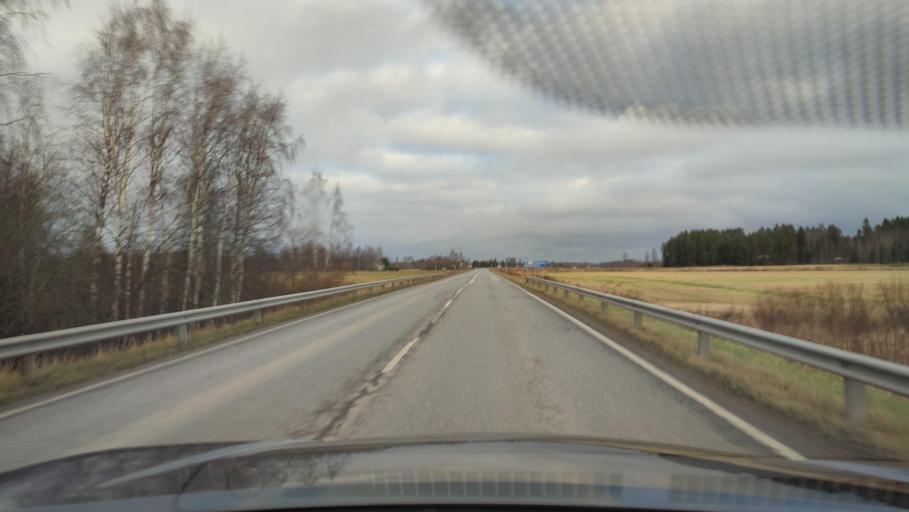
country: FI
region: Southern Ostrobothnia
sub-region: Suupohja
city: Kauhajoki
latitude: 62.3667
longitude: 22.0752
